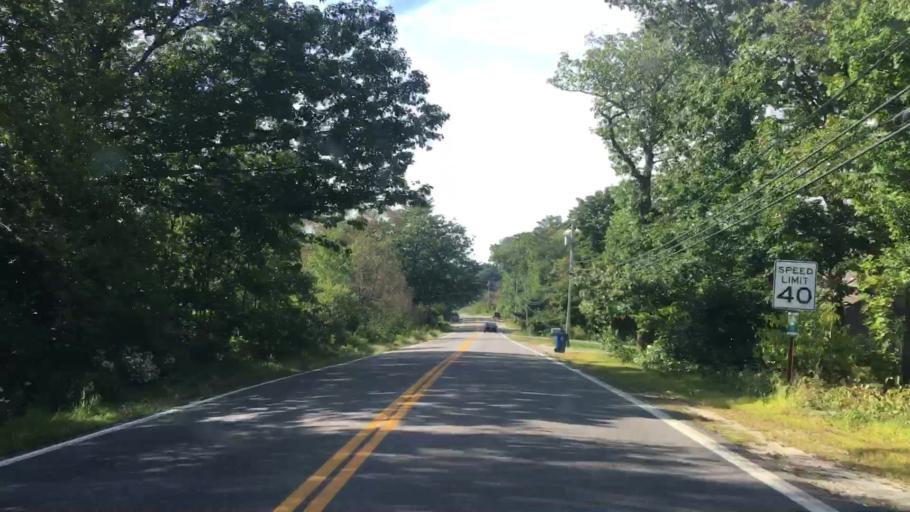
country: US
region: Maine
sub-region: Sagadahoc County
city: Bath
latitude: 43.9296
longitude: -69.8581
